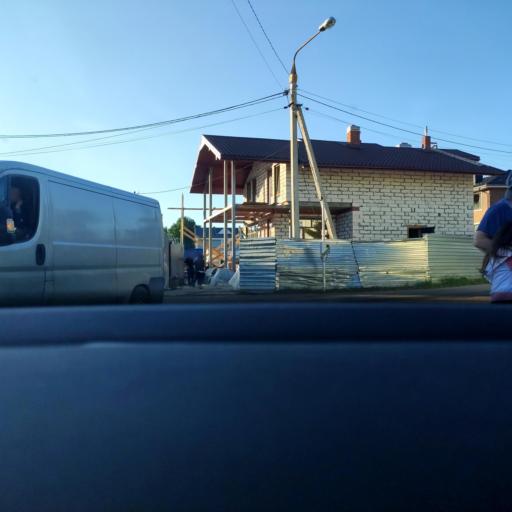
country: RU
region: Moscow
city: Lianozovo
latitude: 55.9283
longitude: 37.6124
